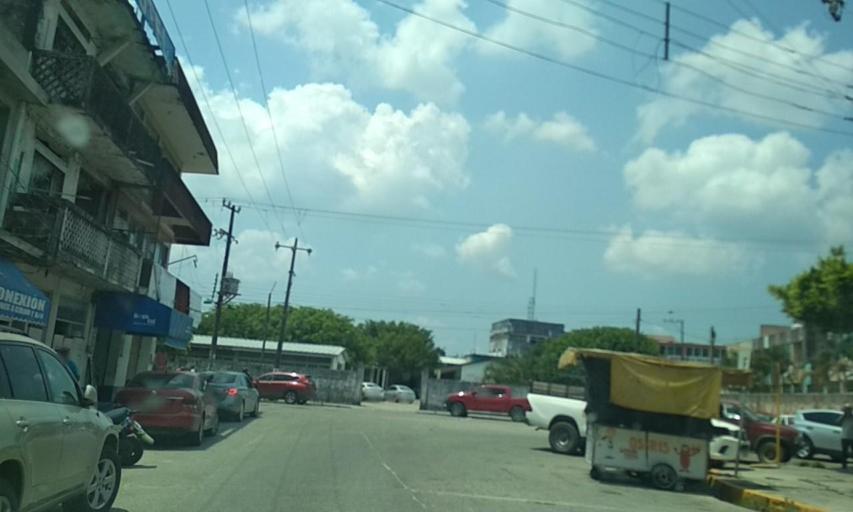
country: MX
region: Veracruz
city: Las Choapas
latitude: 17.9081
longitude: -94.0900
